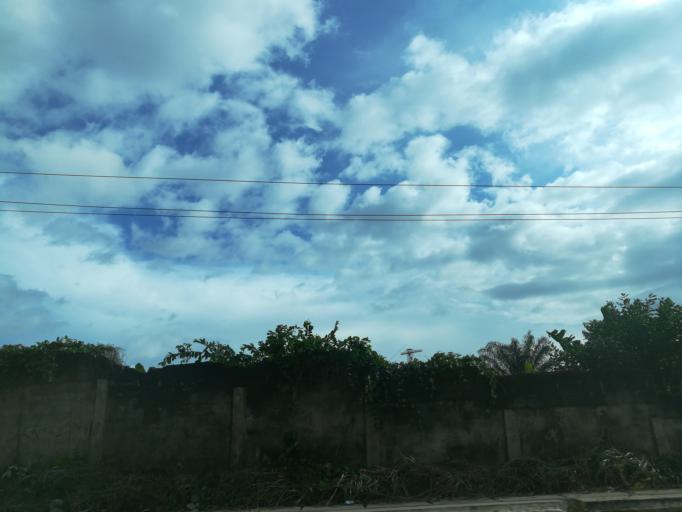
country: NG
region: Lagos
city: Ebute Ikorodu
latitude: 6.5981
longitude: 3.4980
